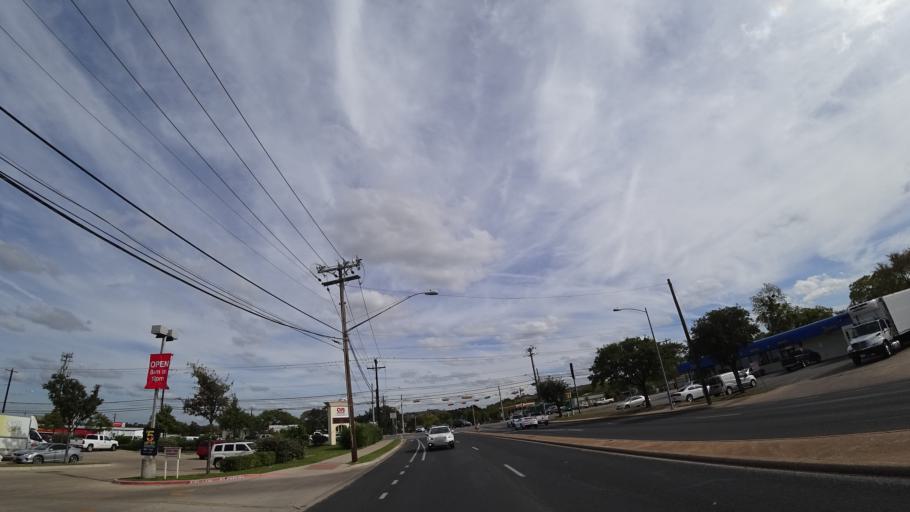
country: US
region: Texas
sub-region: Travis County
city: Onion Creek
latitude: 30.2053
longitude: -97.7755
